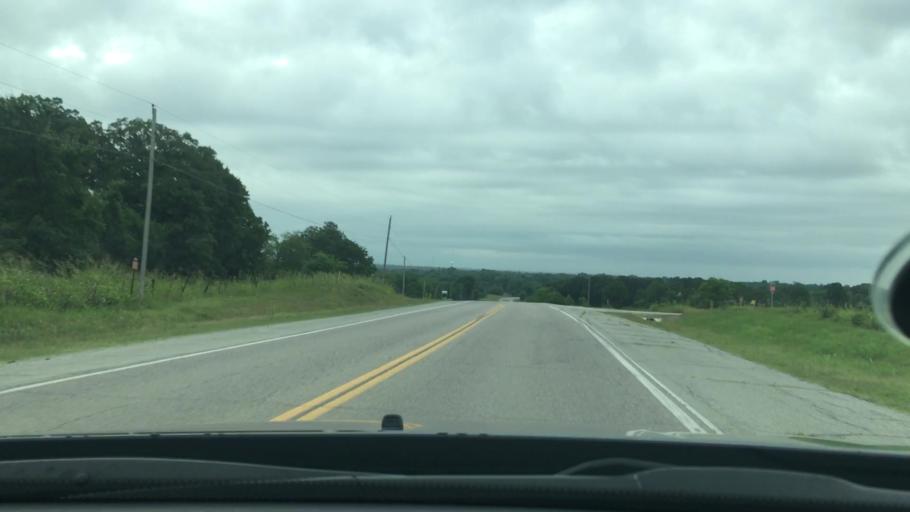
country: US
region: Oklahoma
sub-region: Coal County
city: Coalgate
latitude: 34.5537
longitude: -96.2382
